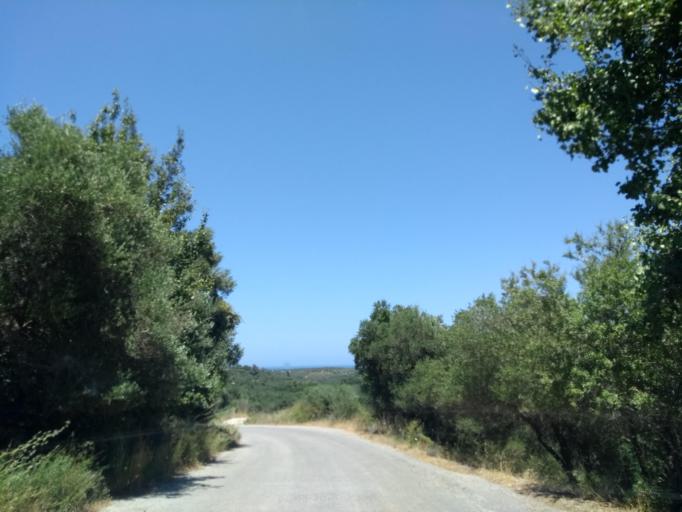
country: GR
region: Crete
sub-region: Nomos Chanias
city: Georgioupolis
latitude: 35.3216
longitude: 24.3131
